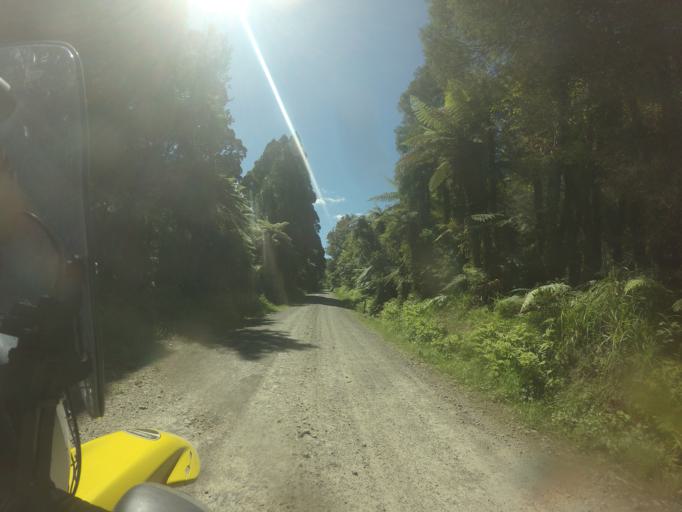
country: NZ
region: Bay of Plenty
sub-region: Opotiki District
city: Opotiki
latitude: -38.2866
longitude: 177.3437
